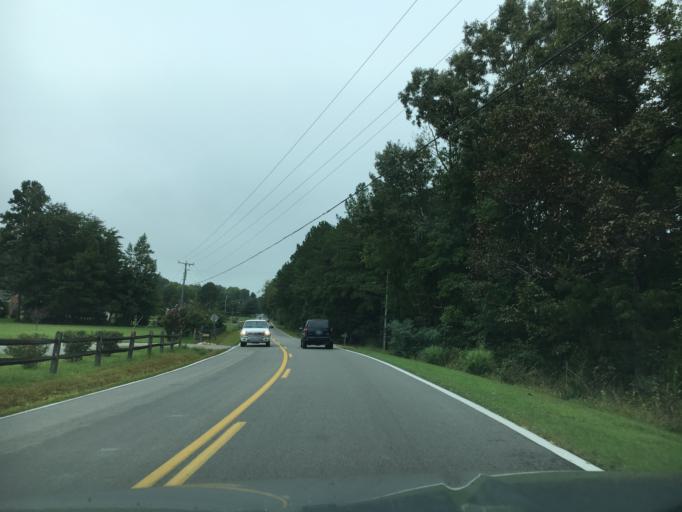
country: US
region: Virginia
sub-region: Powhatan County
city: Powhatan
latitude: 37.4810
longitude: -77.8026
